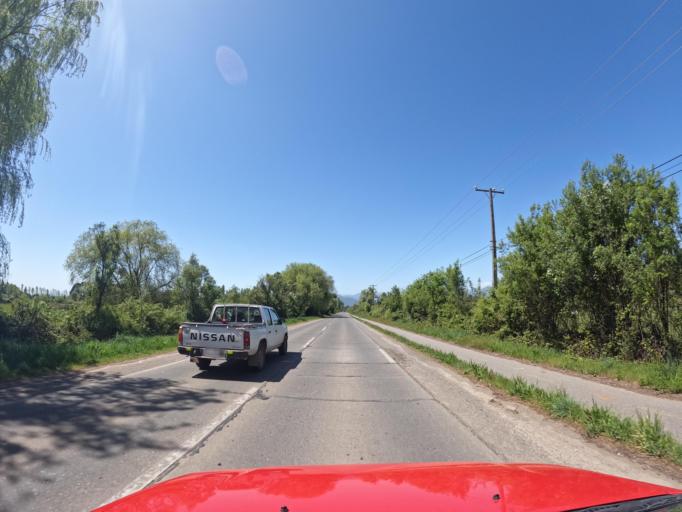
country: CL
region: Maule
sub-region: Provincia de Linares
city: Linares
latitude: -35.8289
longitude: -71.5016
